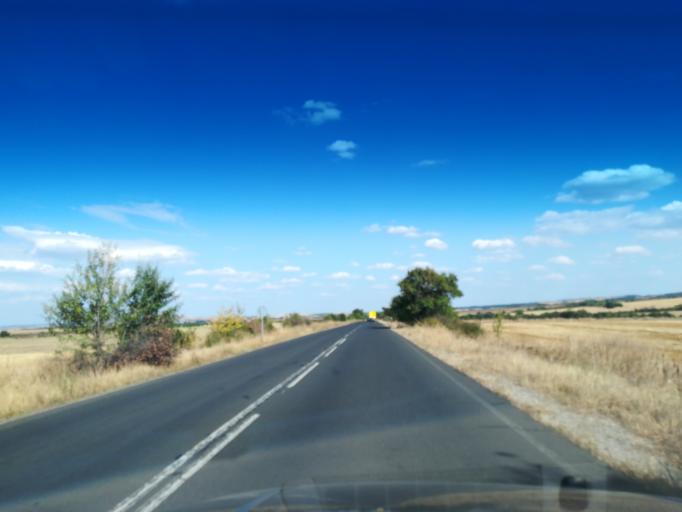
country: BG
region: Stara Zagora
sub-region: Obshtina Chirpan
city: Chirpan
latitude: 42.0579
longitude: 25.2883
